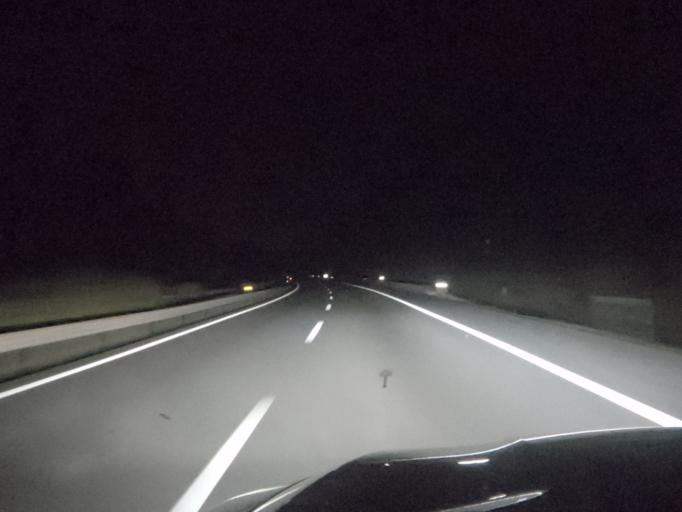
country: PT
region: Aveiro
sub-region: Aveiro
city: Eixo
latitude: 40.6503
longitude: -8.5186
